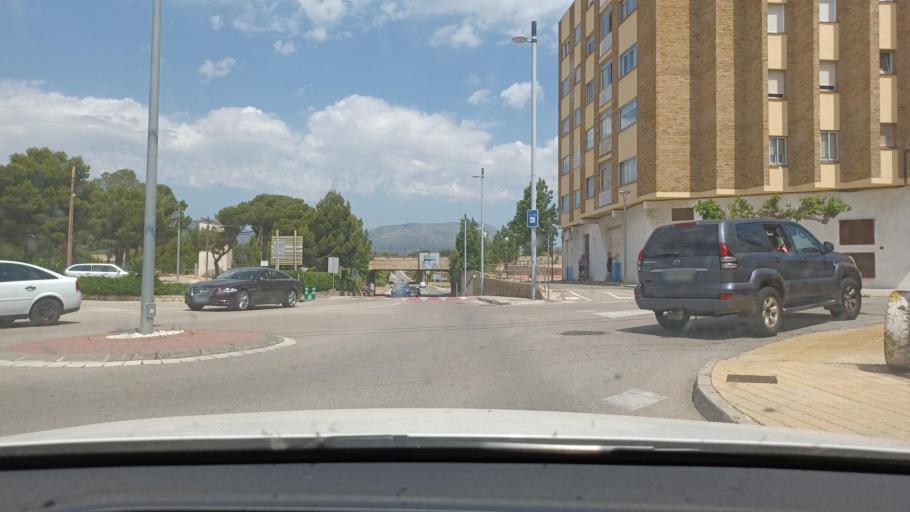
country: ES
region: Catalonia
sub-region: Provincia de Tarragona
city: Colldejou
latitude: 40.9946
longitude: 0.9203
